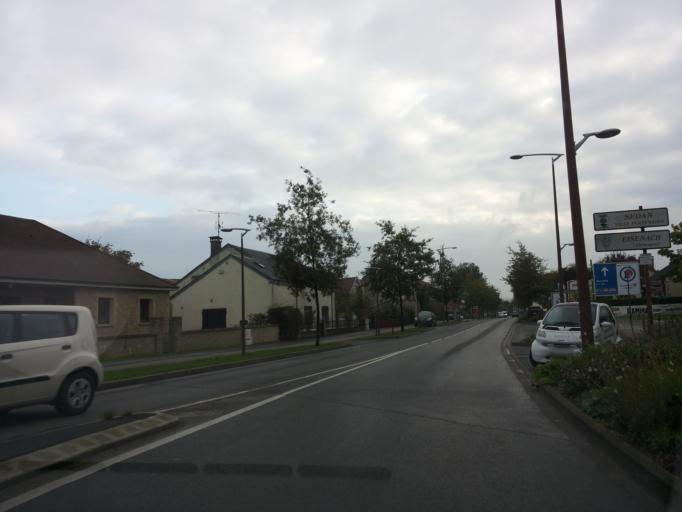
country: FR
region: Champagne-Ardenne
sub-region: Departement des Ardennes
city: Floing
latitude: 49.6948
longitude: 4.9089
